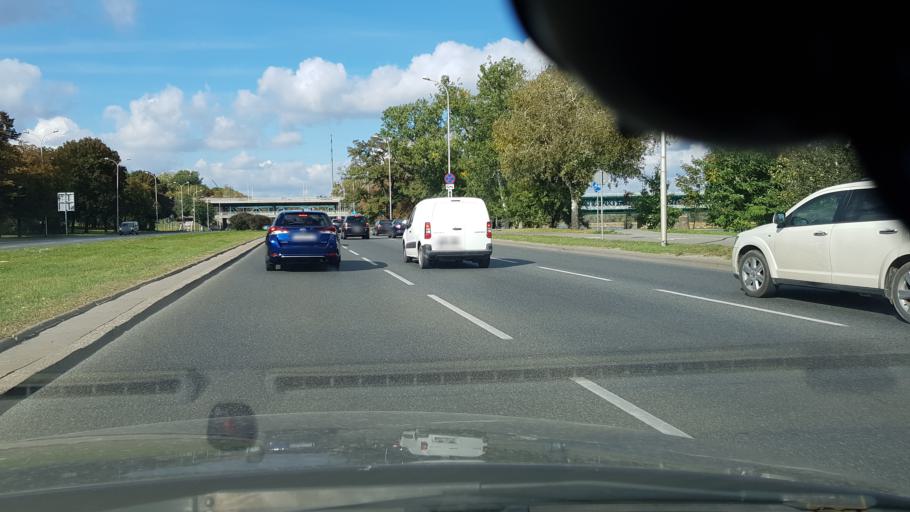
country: PL
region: Masovian Voivodeship
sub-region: Warszawa
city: Praga Polnoc
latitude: 52.2576
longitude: 21.0095
